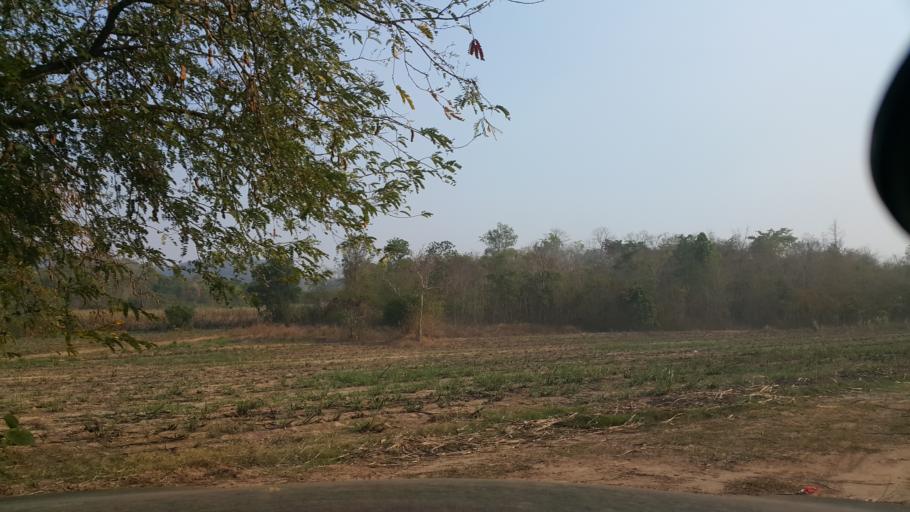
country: TH
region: Sukhothai
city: Thung Saliam
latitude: 17.3394
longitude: 99.4678
